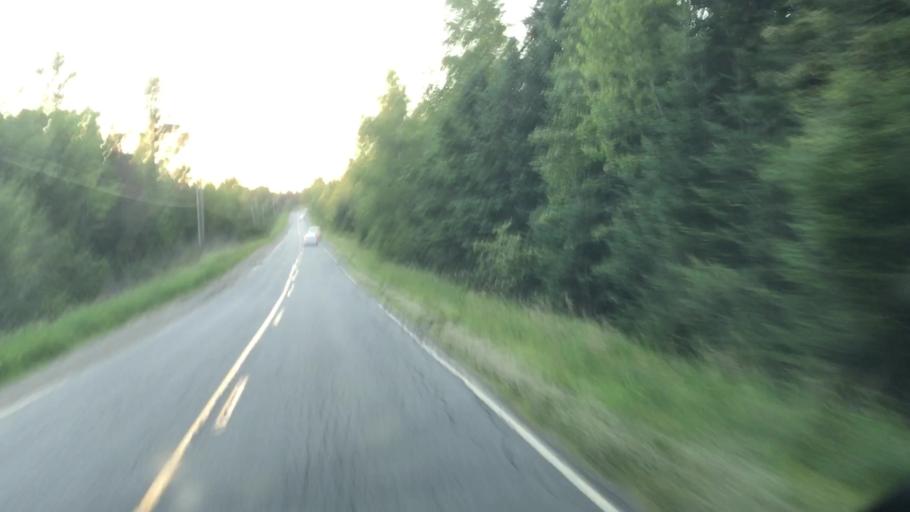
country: US
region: Maine
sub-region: Penobscot County
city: Medway
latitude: 45.6012
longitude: -68.2495
